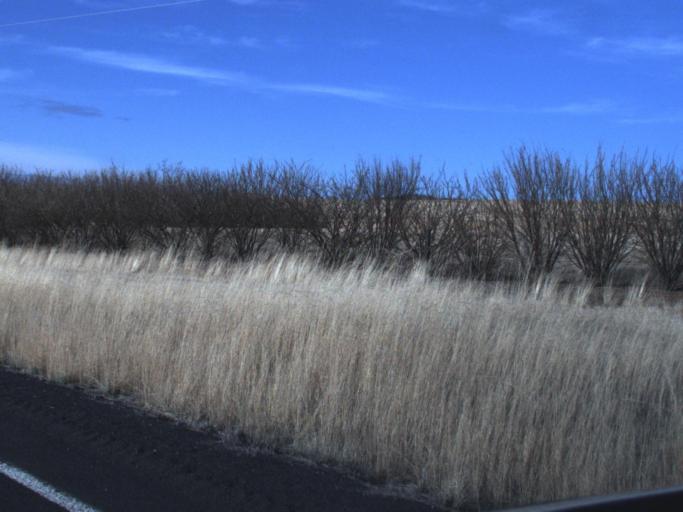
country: US
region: Washington
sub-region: Lincoln County
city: Davenport
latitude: 47.8608
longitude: -118.2176
